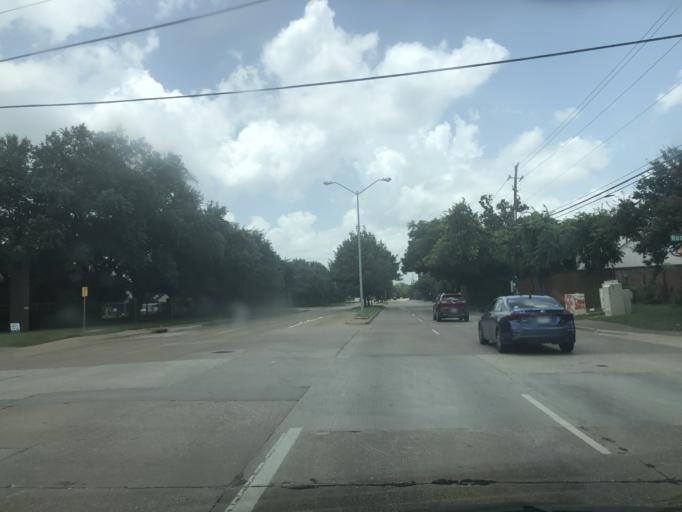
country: US
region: Texas
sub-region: Dallas County
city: University Park
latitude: 32.8666
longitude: -96.8376
